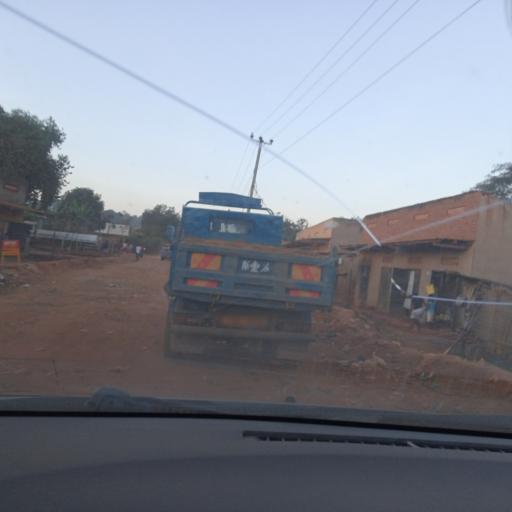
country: UG
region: Central Region
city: Masaka
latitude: -0.3211
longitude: 31.7649
